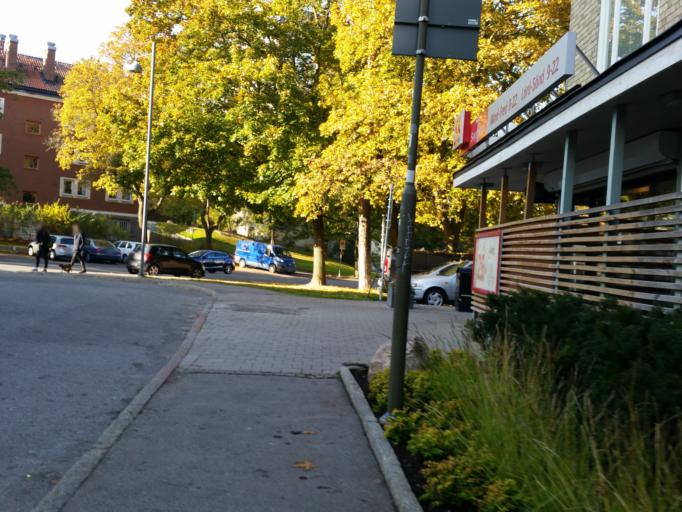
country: SE
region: Stockholm
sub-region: Solna Kommun
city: Rasunda
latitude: 59.3679
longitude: 17.9799
